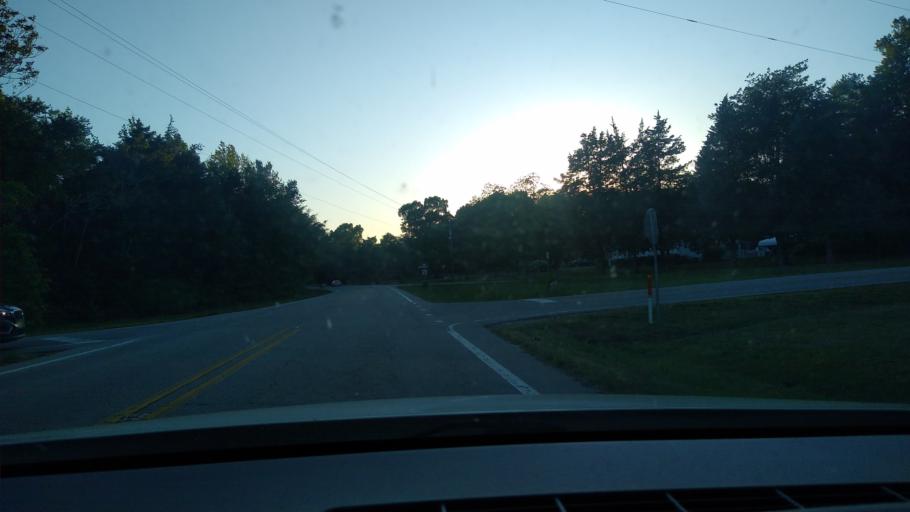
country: US
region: North Carolina
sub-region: Rockingham County
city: Reidsville
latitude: 36.3934
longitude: -79.5544
